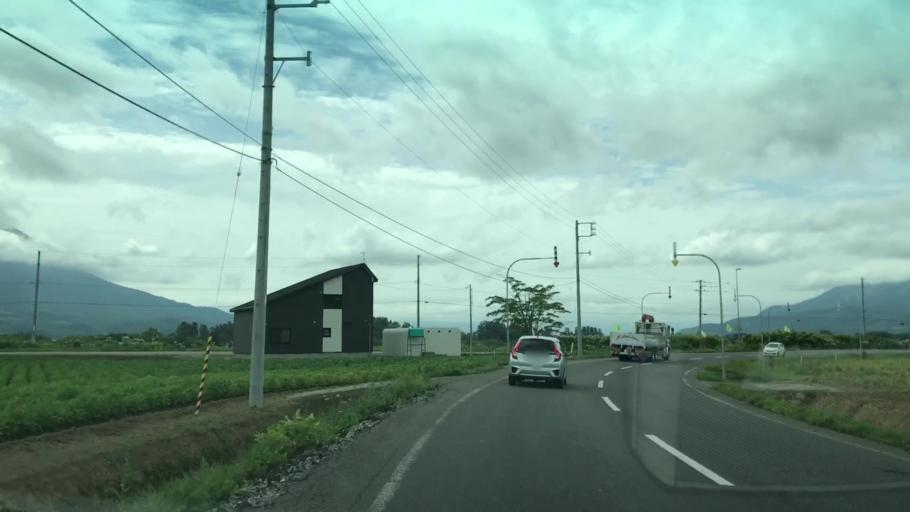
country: JP
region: Hokkaido
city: Niseko Town
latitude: 42.9325
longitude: 140.8027
